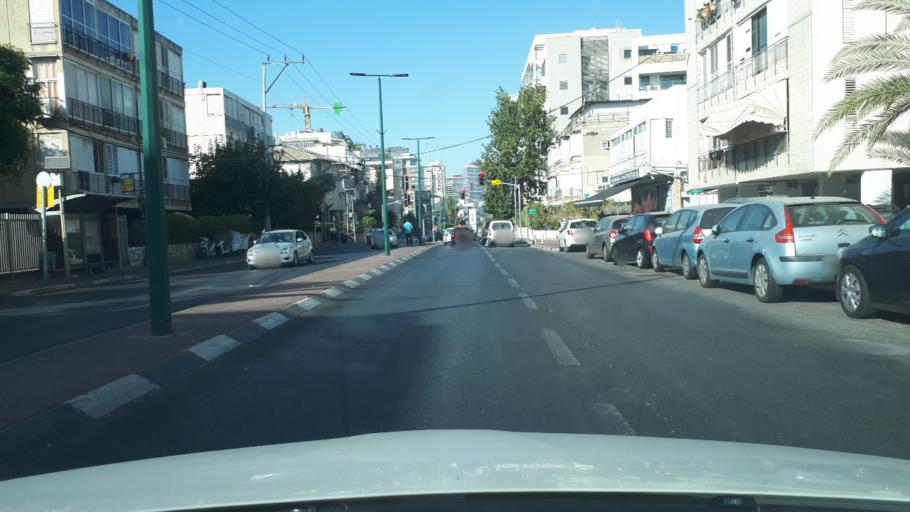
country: IL
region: Tel Aviv
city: Ramat Gan
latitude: 32.0796
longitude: 34.8198
